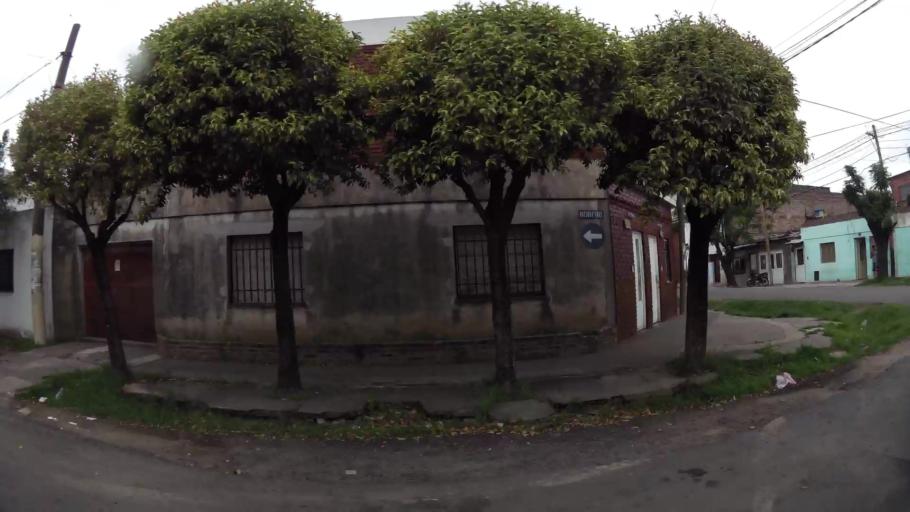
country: AR
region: Santa Fe
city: Gobernador Galvez
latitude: -32.9991
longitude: -60.6621
